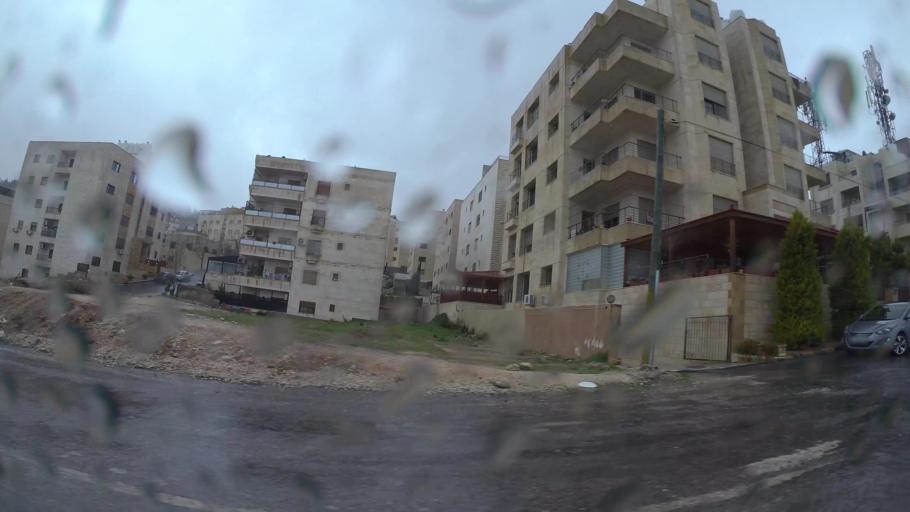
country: JO
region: Amman
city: Al Jubayhah
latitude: 32.0211
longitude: 35.8925
